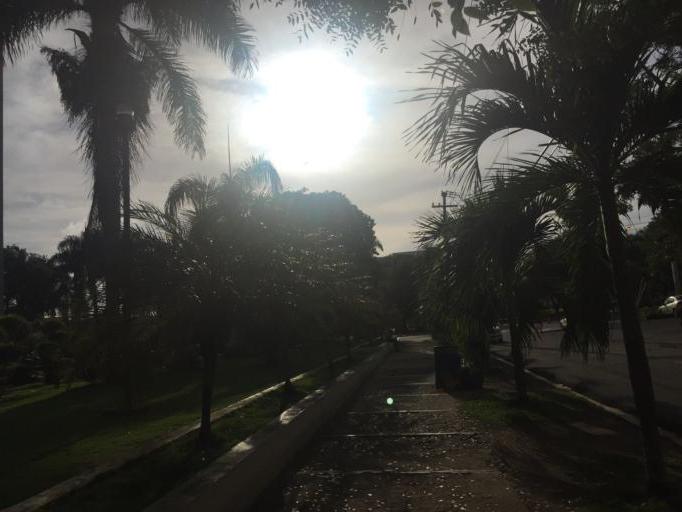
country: DO
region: Nacional
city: La Julia
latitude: 18.4616
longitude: -69.9184
